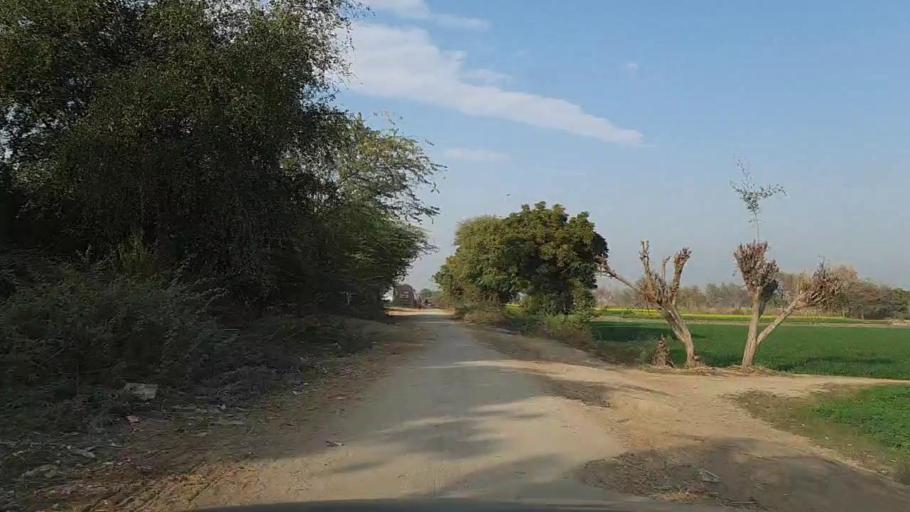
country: PK
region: Sindh
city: Daur
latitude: 26.4152
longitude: 68.4334
